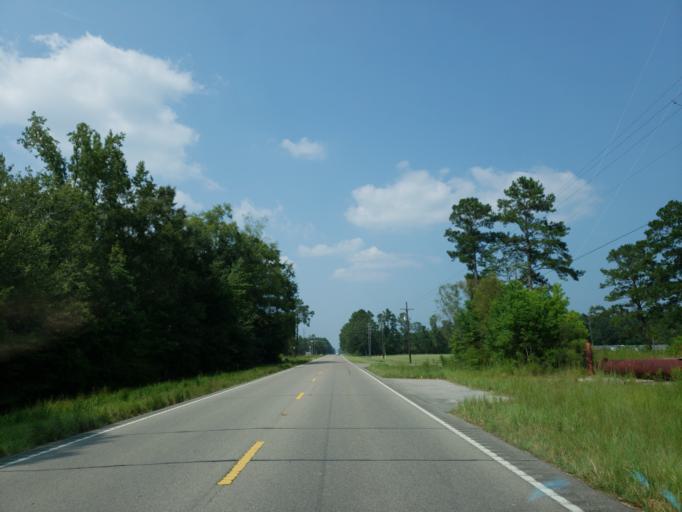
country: US
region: Mississippi
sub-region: Forrest County
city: Glendale
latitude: 31.4515
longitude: -89.2858
